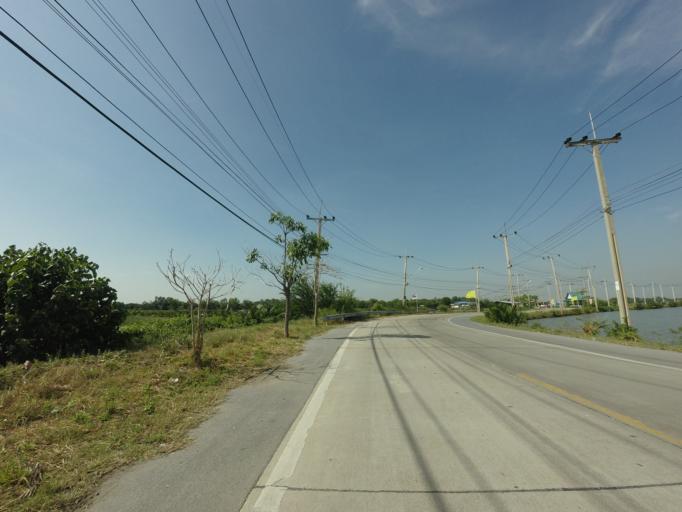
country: TH
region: Samut Prakan
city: Phra Samut Chedi
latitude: 13.5441
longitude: 100.5194
